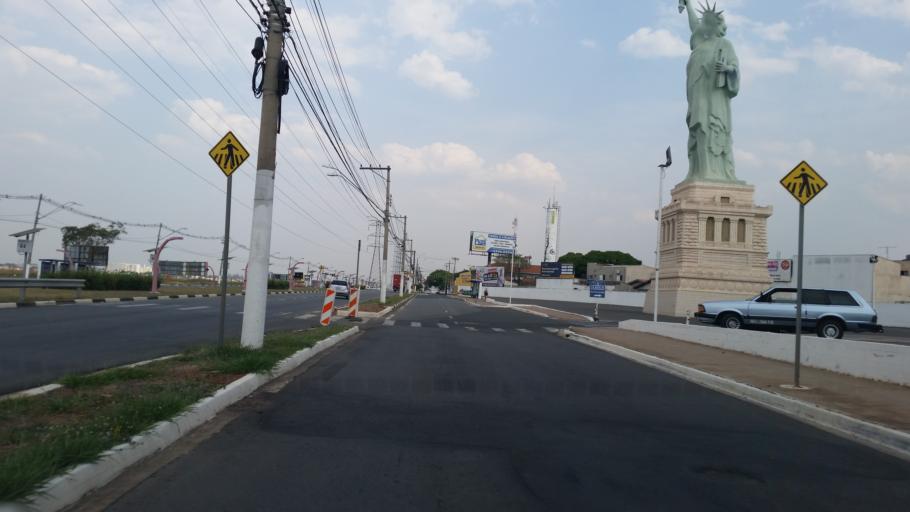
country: BR
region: Sao Paulo
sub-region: Hortolandia
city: Hortolandia
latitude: -22.8868
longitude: -47.1937
